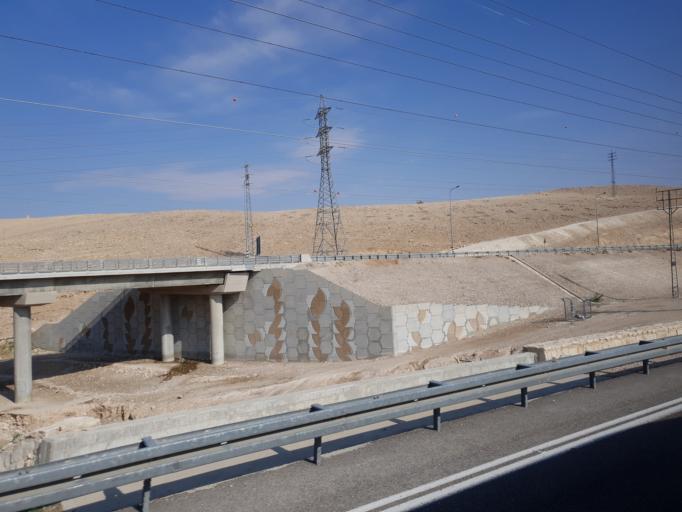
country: PS
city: Az Za`ayyim
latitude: 31.8078
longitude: 35.3306
